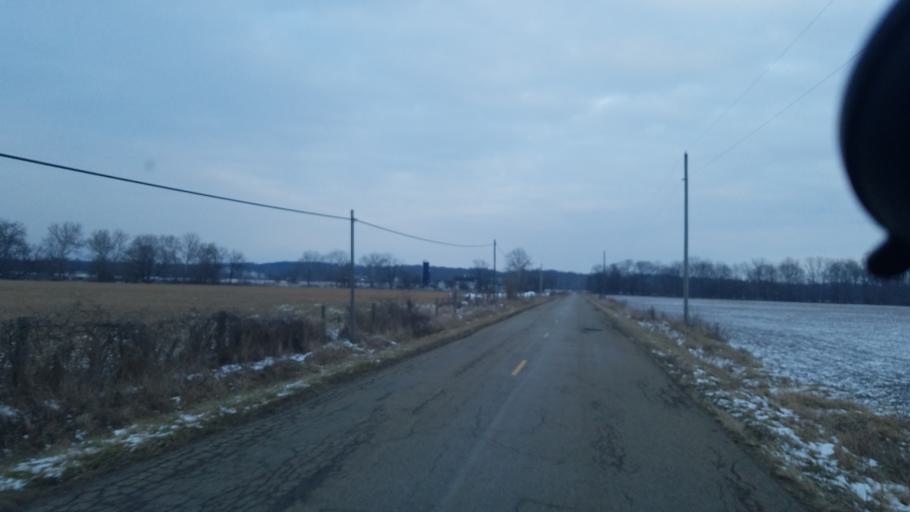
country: US
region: Ohio
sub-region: Knox County
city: Mount Vernon
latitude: 40.4261
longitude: -82.5226
